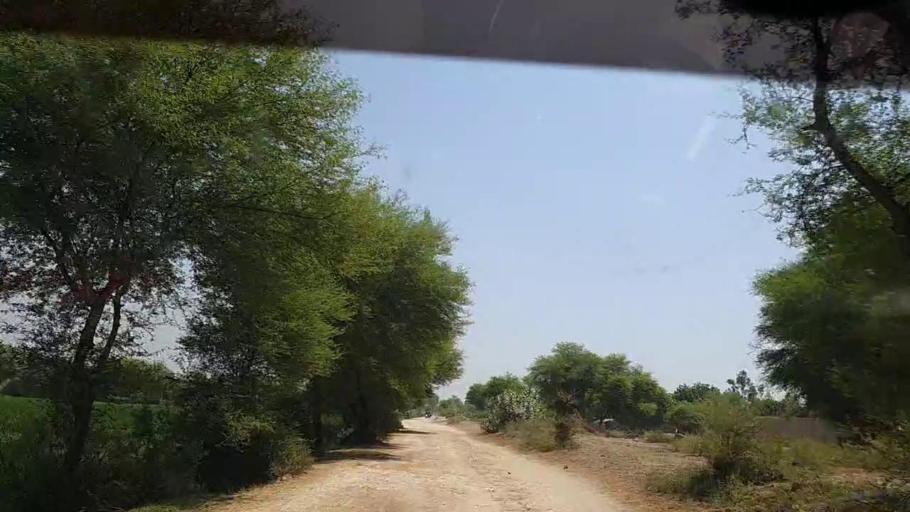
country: PK
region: Sindh
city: Ghauspur
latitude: 28.1691
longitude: 69.1213
